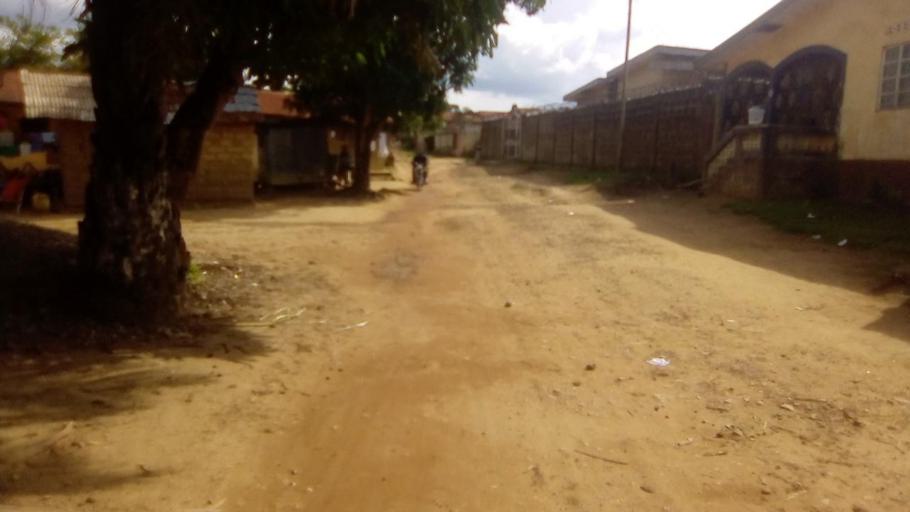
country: SL
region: Southern Province
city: Bo
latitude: 7.9506
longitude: -11.7223
